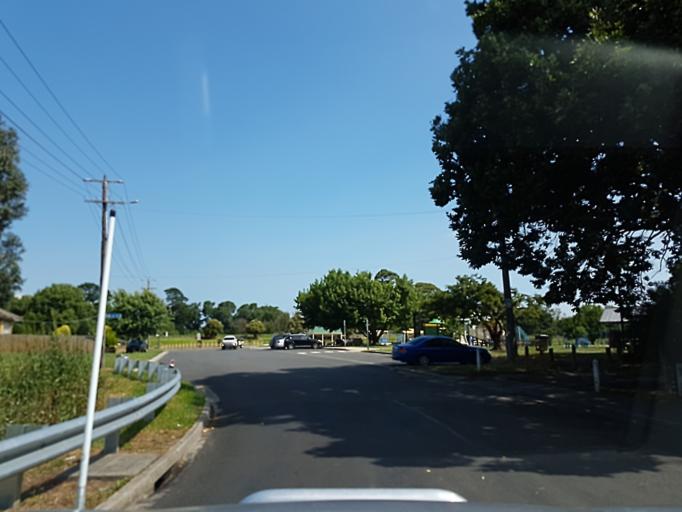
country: AU
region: Victoria
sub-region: Latrobe
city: Traralgon
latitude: -38.1958
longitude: 146.5451
